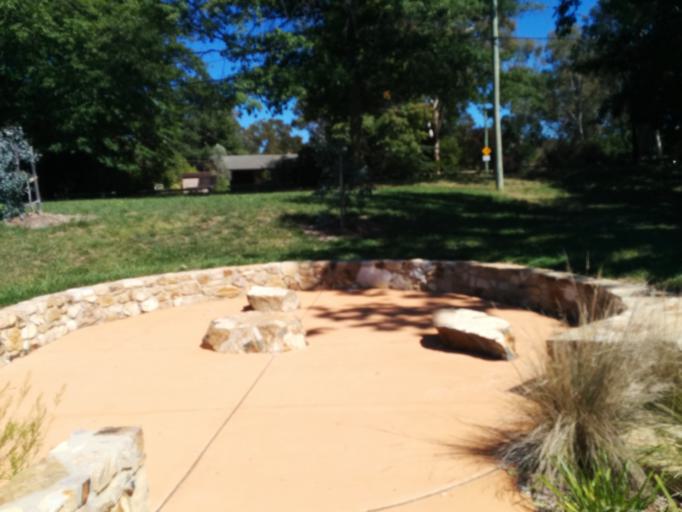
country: AU
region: Australian Capital Territory
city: Acton
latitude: -35.2552
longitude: 149.1298
